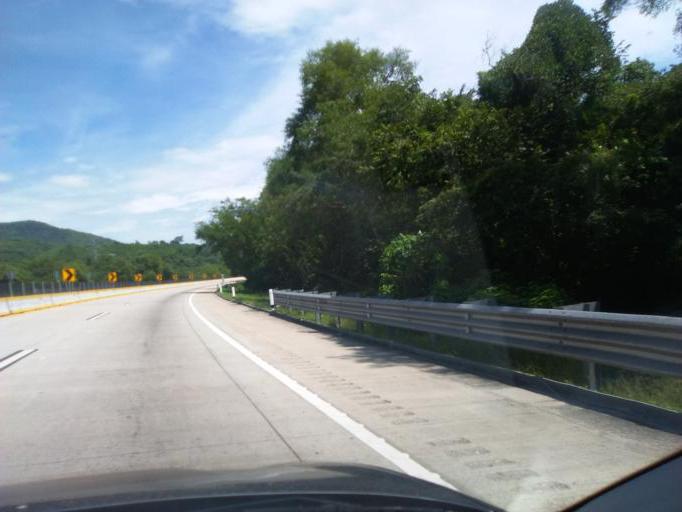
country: MX
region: Guerrero
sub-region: Acapulco de Juarez
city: Kilometro 30
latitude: 16.9975
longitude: -99.6962
